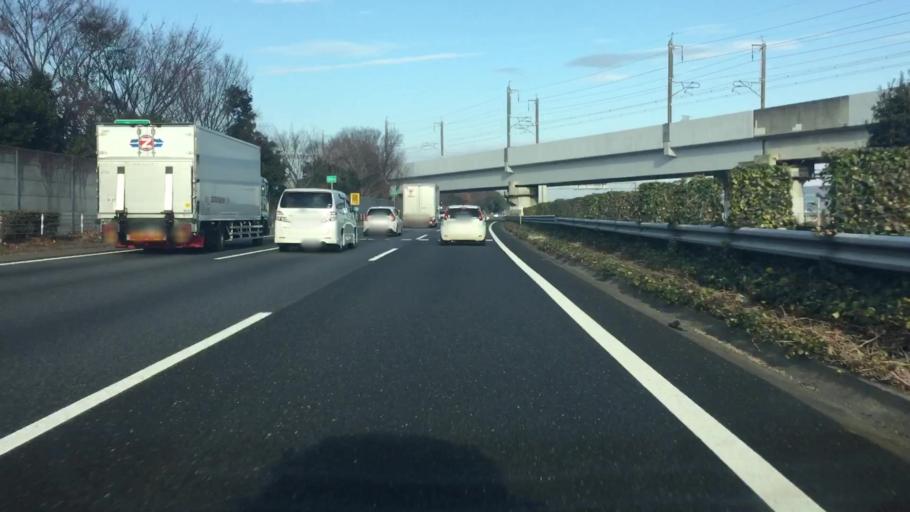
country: JP
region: Saitama
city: Honjo
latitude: 36.2327
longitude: 139.1498
